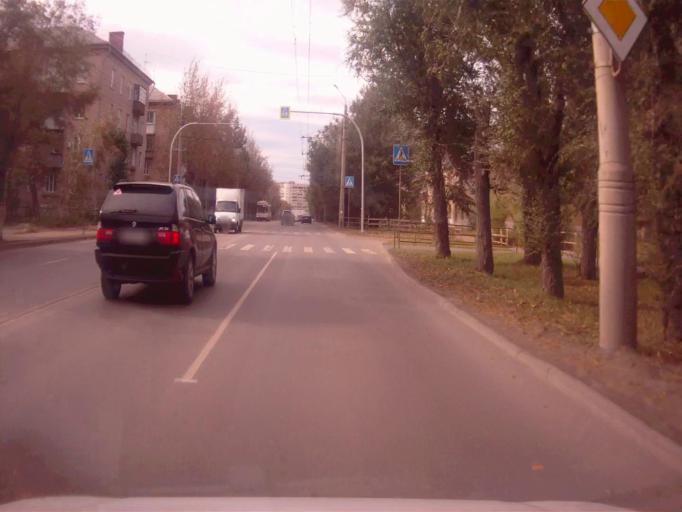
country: RU
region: Chelyabinsk
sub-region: Gorod Chelyabinsk
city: Chelyabinsk
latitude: 55.1151
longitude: 61.4510
